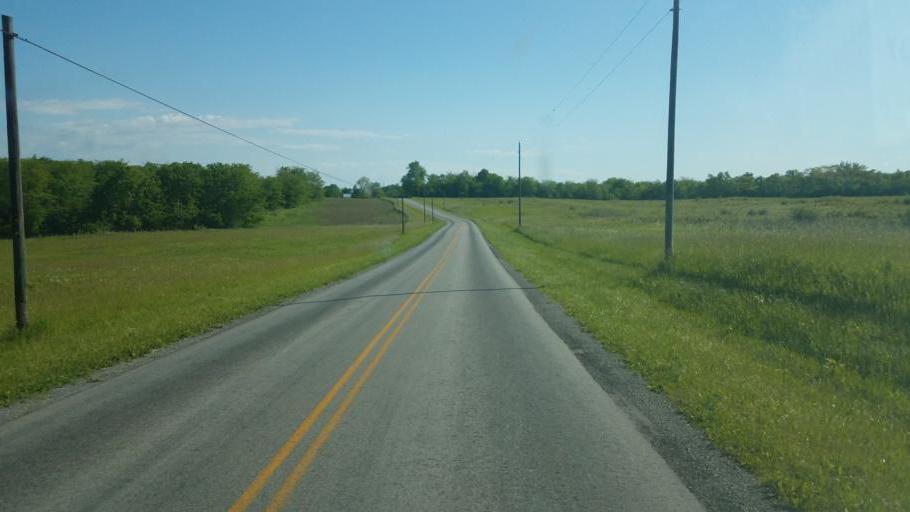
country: US
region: Ohio
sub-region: Hardin County
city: Kenton
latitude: 40.5881
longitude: -83.6203
